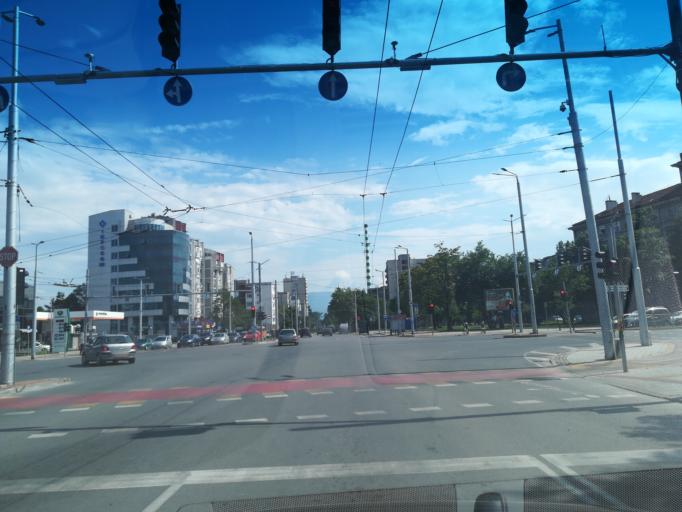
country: BG
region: Plovdiv
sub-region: Obshtina Plovdiv
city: Plovdiv
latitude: 42.1473
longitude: 24.7631
